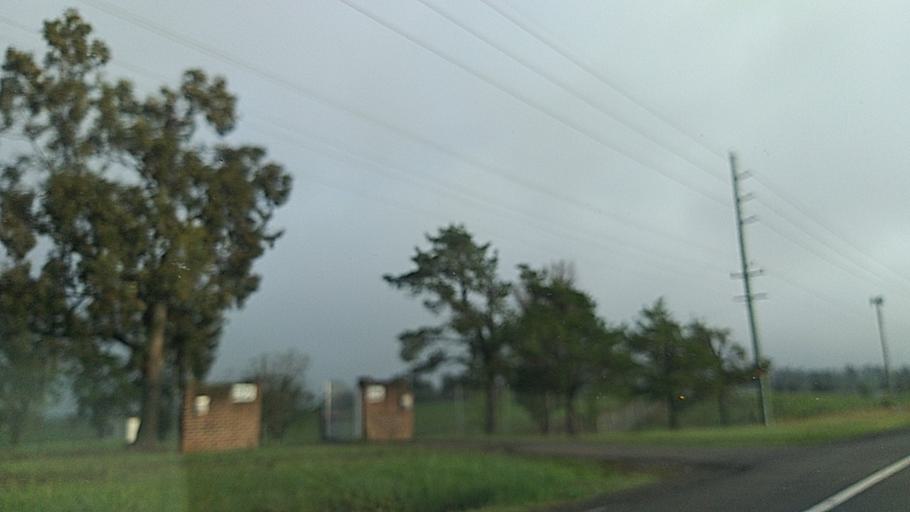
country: AU
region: New South Wales
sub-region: Penrith Municipality
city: Glenmore Park
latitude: -33.8156
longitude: 150.6891
